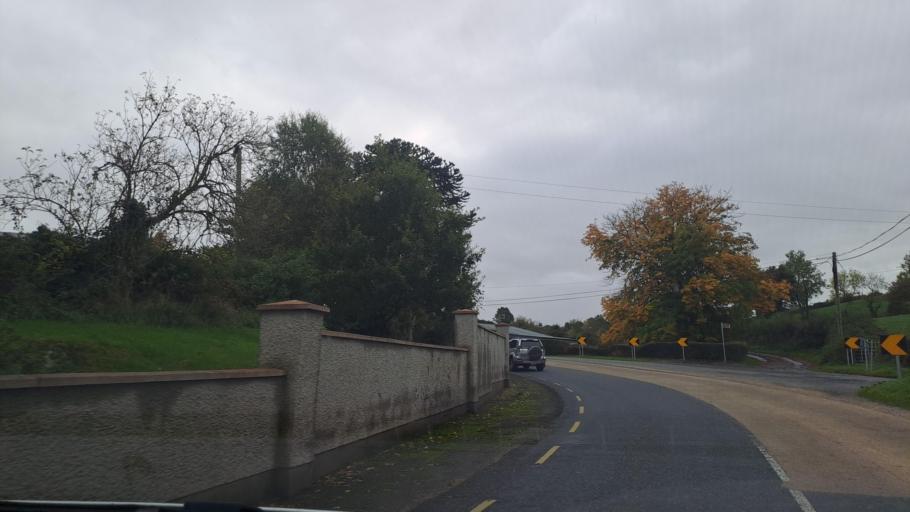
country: IE
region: Ulster
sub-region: An Cabhan
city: Cootehill
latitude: 54.0408
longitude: -7.0478
